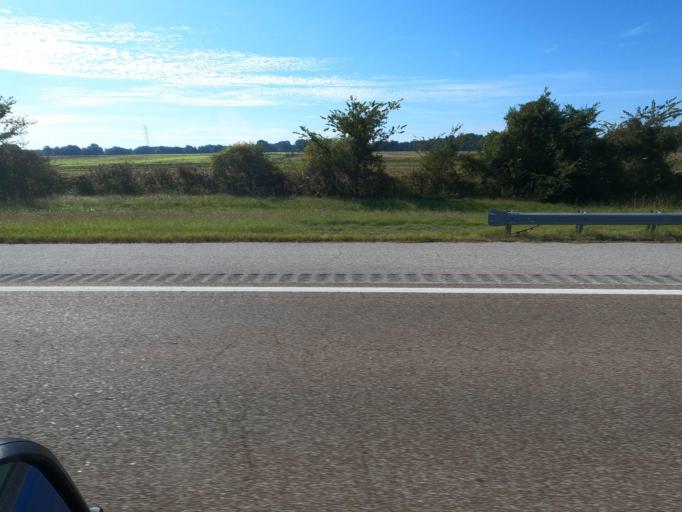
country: US
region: Tennessee
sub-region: Shelby County
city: Millington
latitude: 35.3103
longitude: -89.8544
